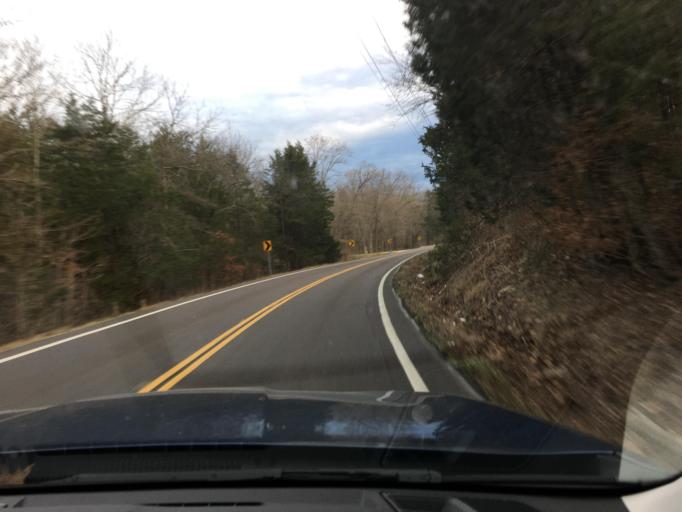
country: US
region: Missouri
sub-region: Jefferson County
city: De Soto
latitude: 38.1066
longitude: -90.5604
